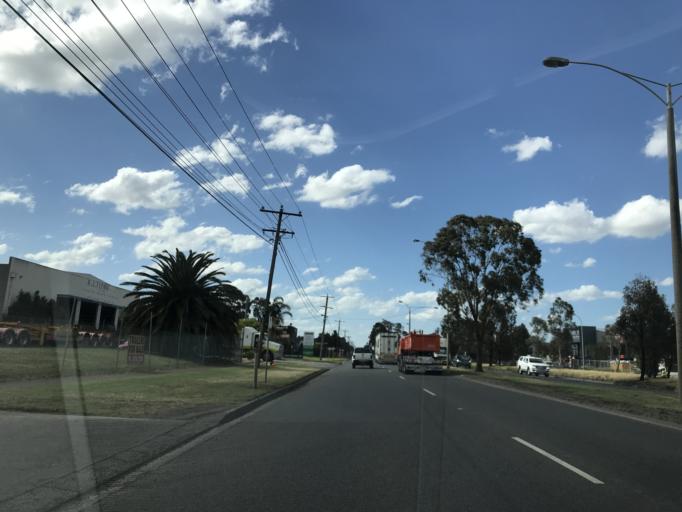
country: AU
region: Victoria
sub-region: Brimbank
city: Sunshine West
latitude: -37.8144
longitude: 144.8172
